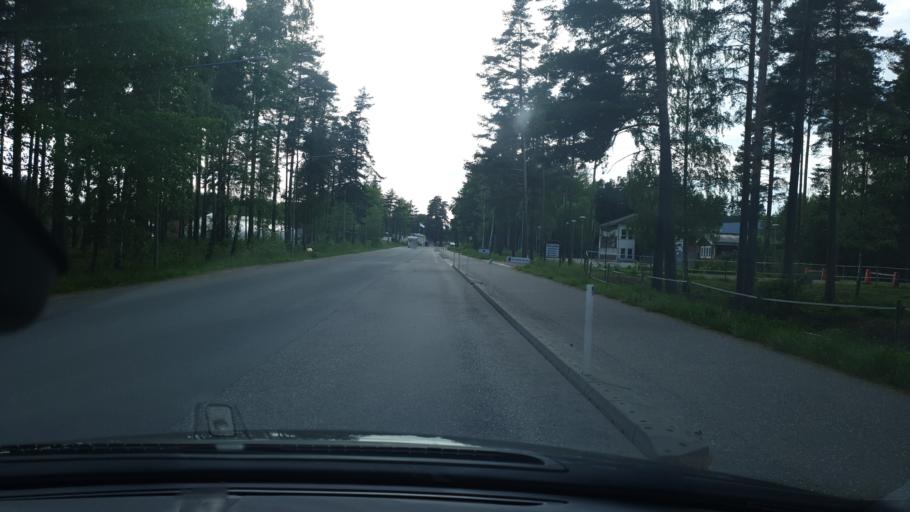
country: SE
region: Joenkoeping
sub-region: Vetlanda Kommun
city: Vetlanda
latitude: 57.4200
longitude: 15.1077
